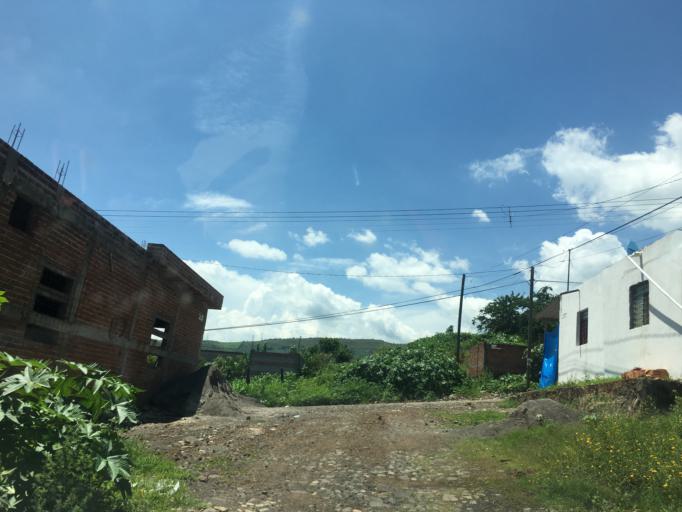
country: MX
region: Nayarit
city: Ixtlan del Rio
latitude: 21.0360
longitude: -104.3526
